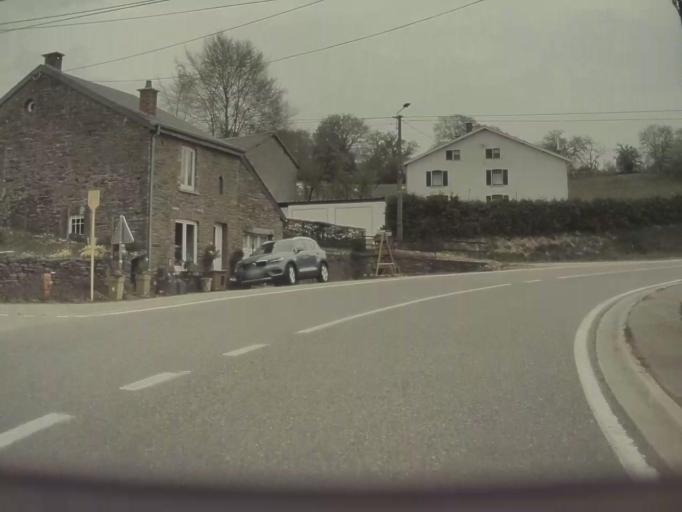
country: BE
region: Wallonia
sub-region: Province de Liege
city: Lierneux
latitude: 50.3298
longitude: 5.7619
